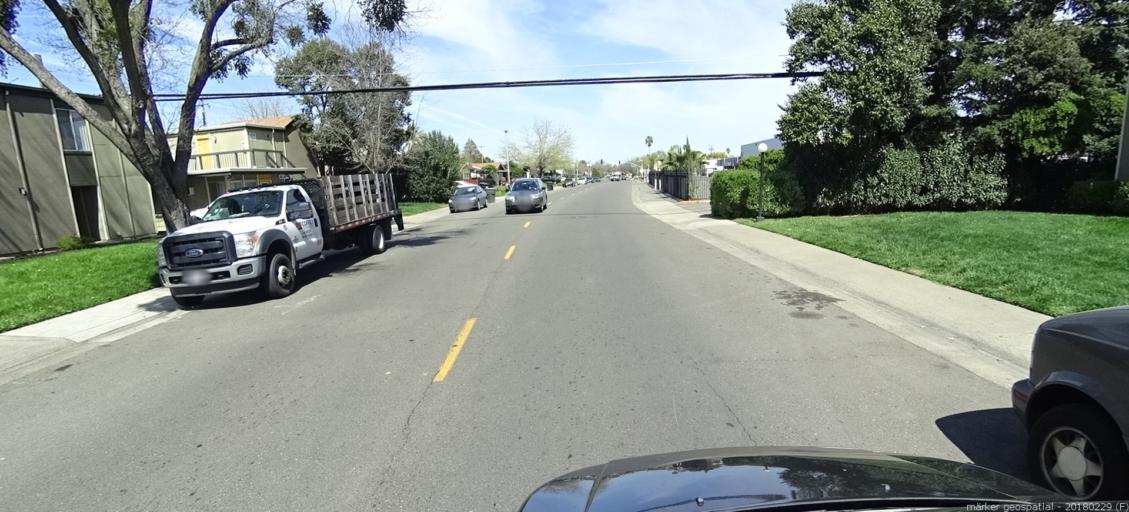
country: US
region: California
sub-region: Sacramento County
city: Rosemont
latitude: 38.5452
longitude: -121.3623
